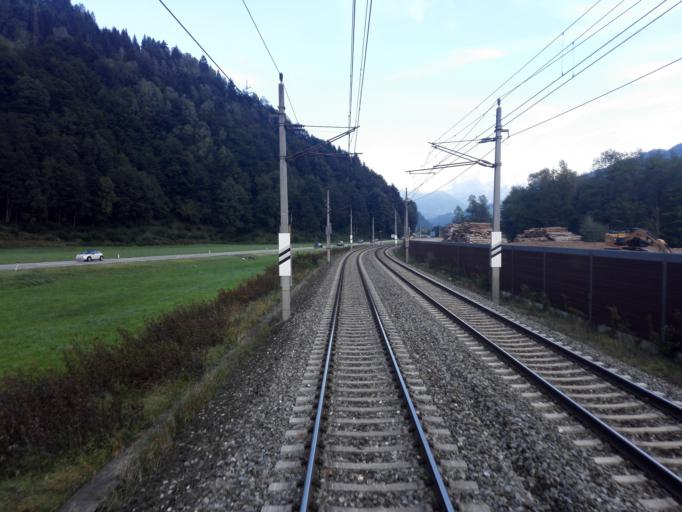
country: AT
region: Salzburg
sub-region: Politischer Bezirk Sankt Johann im Pongau
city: Sankt Johann im Pongau
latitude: 47.3737
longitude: 13.2078
